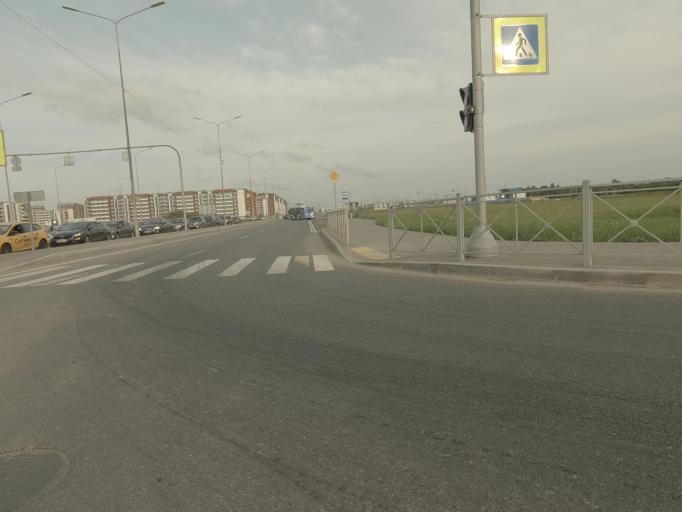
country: RU
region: St.-Petersburg
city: Sosnovaya Polyana
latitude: 59.8405
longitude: 30.0914
